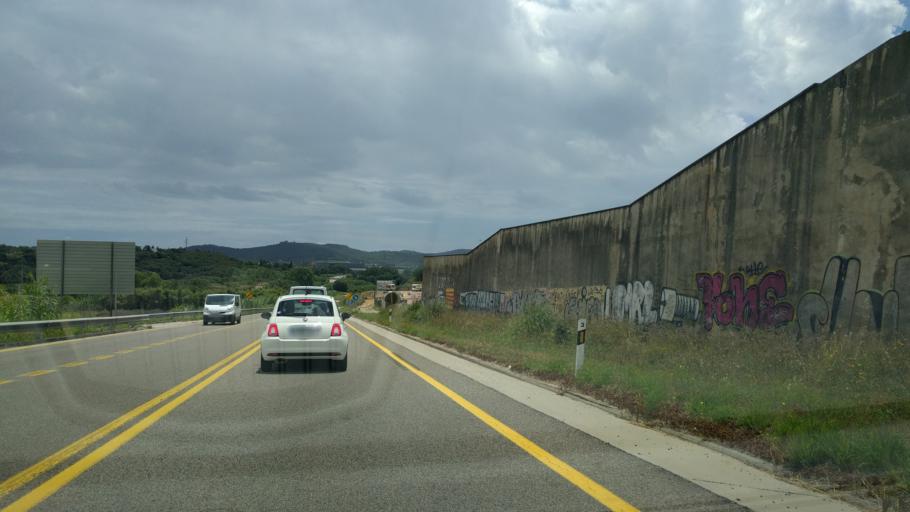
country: ES
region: Catalonia
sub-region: Provincia de Barcelona
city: Tordera
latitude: 41.7131
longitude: 2.7305
